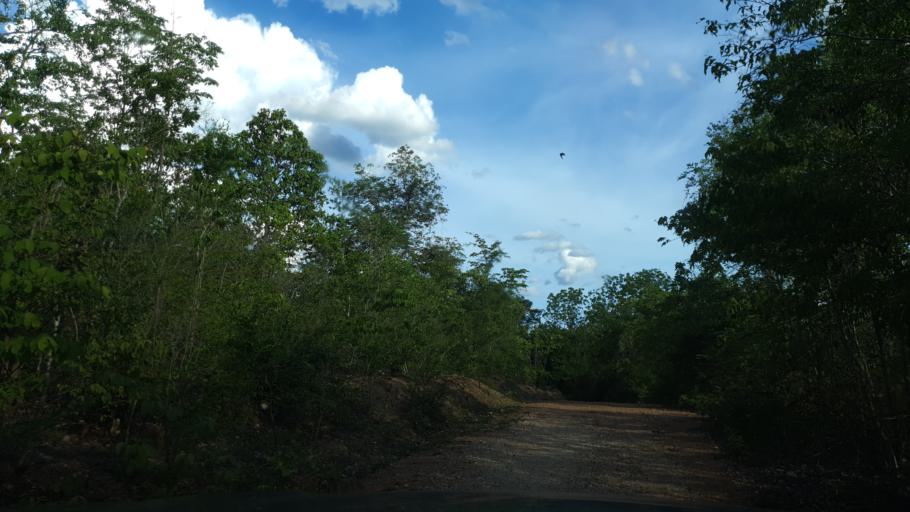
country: TH
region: Lampang
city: Sop Prap
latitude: 17.8859
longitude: 99.2914
